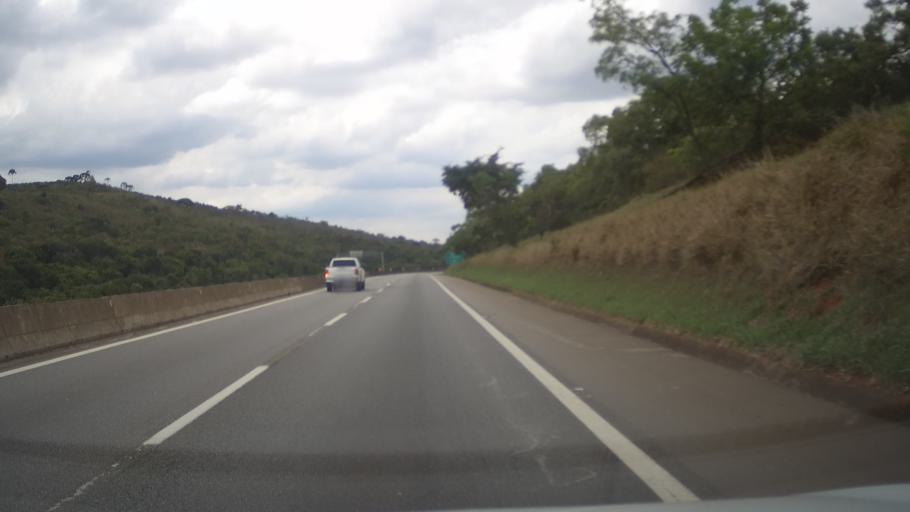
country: BR
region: Minas Gerais
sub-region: Tres Coracoes
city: Tres Coracoes
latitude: -21.5305
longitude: -45.2307
